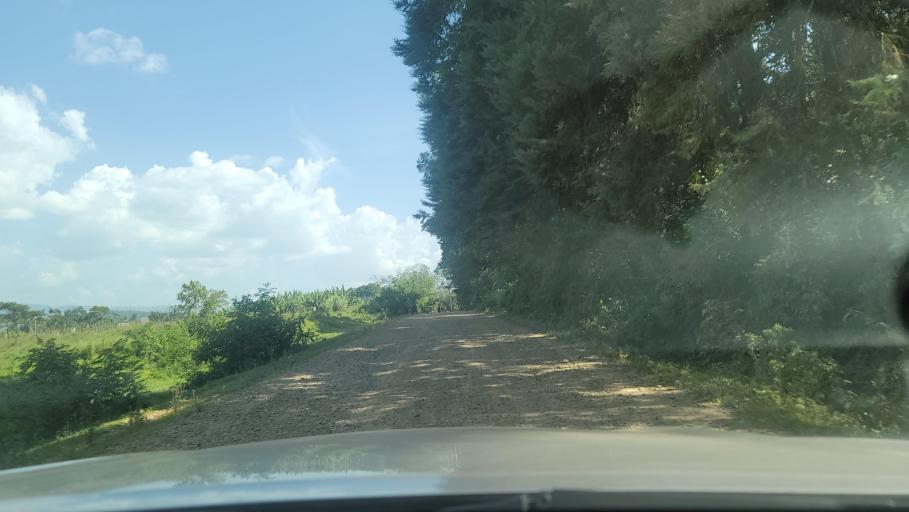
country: ET
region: Oromiya
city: Agaro
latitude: 7.7904
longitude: 36.4305
